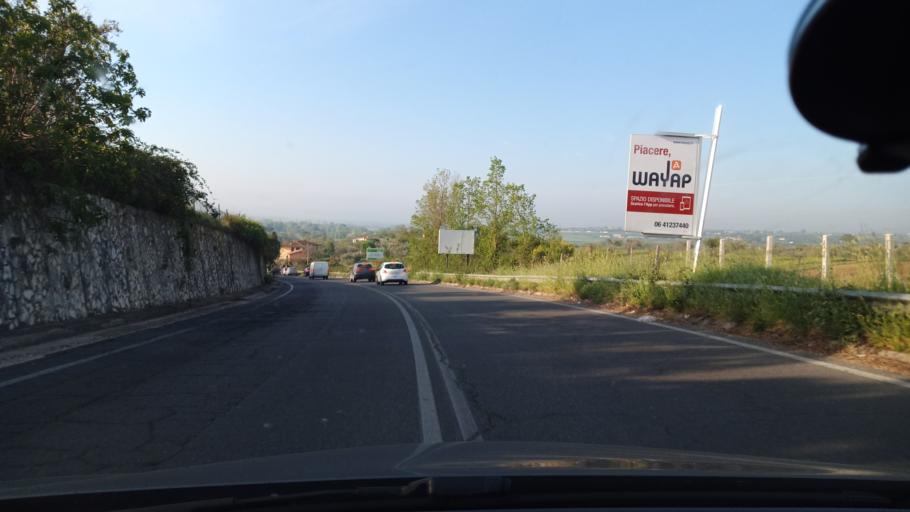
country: IT
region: Latium
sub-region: Citta metropolitana di Roma Capitale
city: Fiano Romano
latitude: 42.1808
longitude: 12.6359
